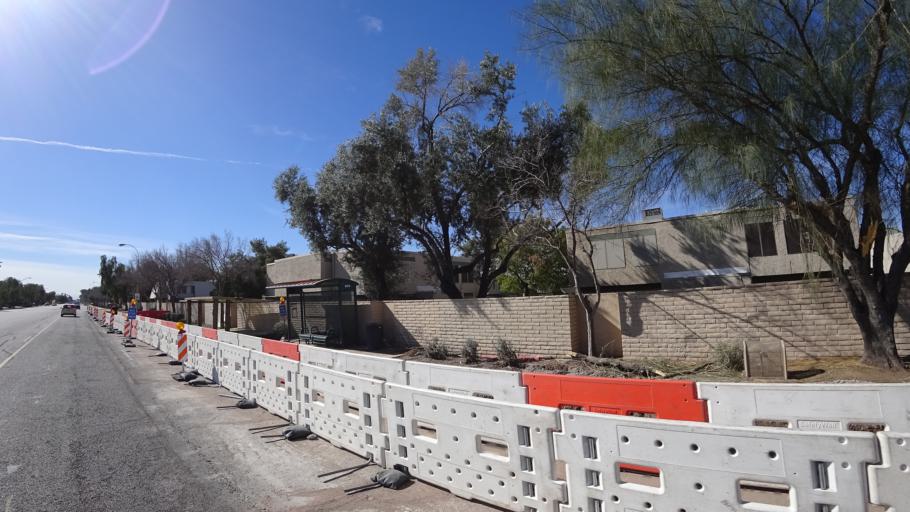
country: US
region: Arizona
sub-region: Maricopa County
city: Glendale
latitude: 33.5665
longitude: -112.1863
